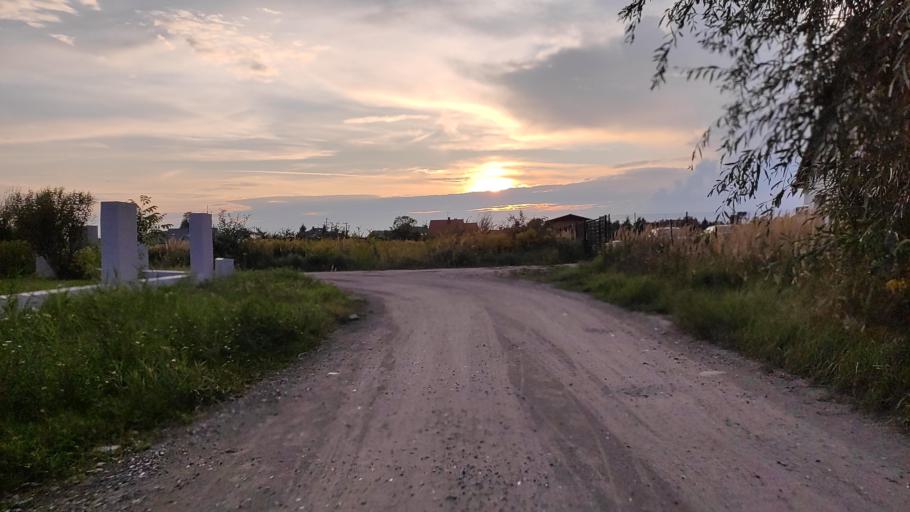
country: PL
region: Greater Poland Voivodeship
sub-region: Powiat poznanski
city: Kleszczewo
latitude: 52.3910
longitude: 17.1623
